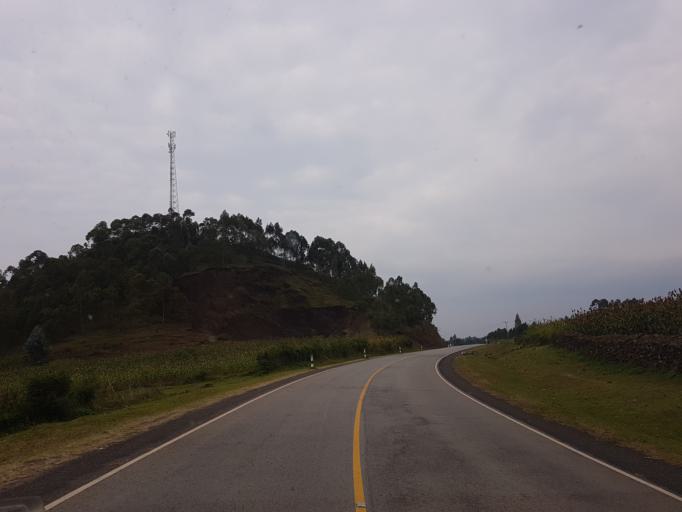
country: UG
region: Western Region
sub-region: Kisoro District
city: Kisoro
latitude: -1.3295
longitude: 29.7342
